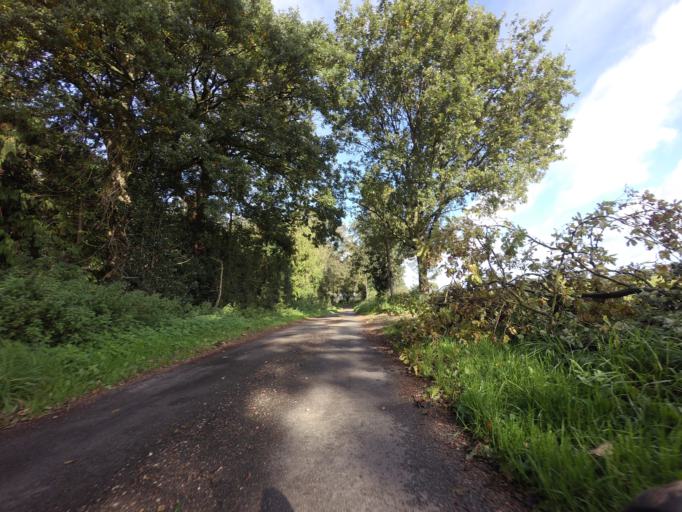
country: GB
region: England
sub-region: Norfolk
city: Fakenham
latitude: 52.8892
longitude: 0.6836
